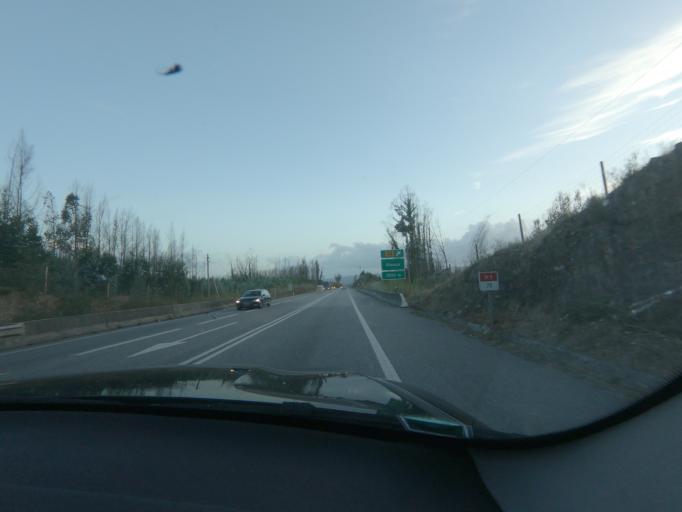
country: PT
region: Viseu
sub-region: Mortagua
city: Mortagua
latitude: 40.3493
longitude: -8.2061
